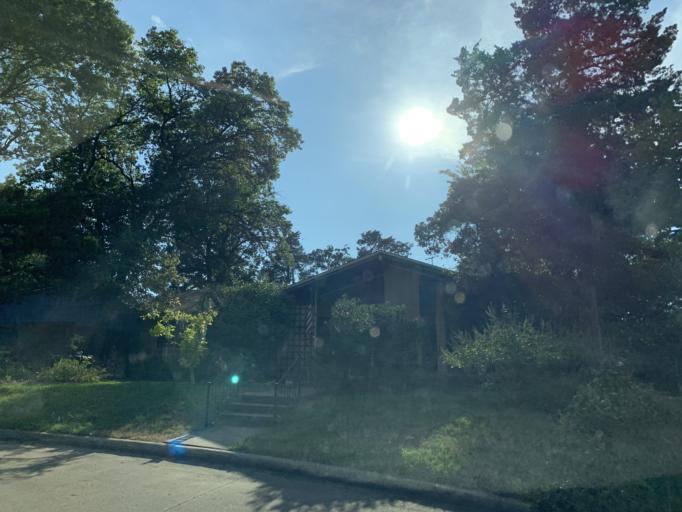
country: US
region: Texas
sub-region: Dallas County
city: Dallas
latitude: 32.7349
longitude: -96.8174
